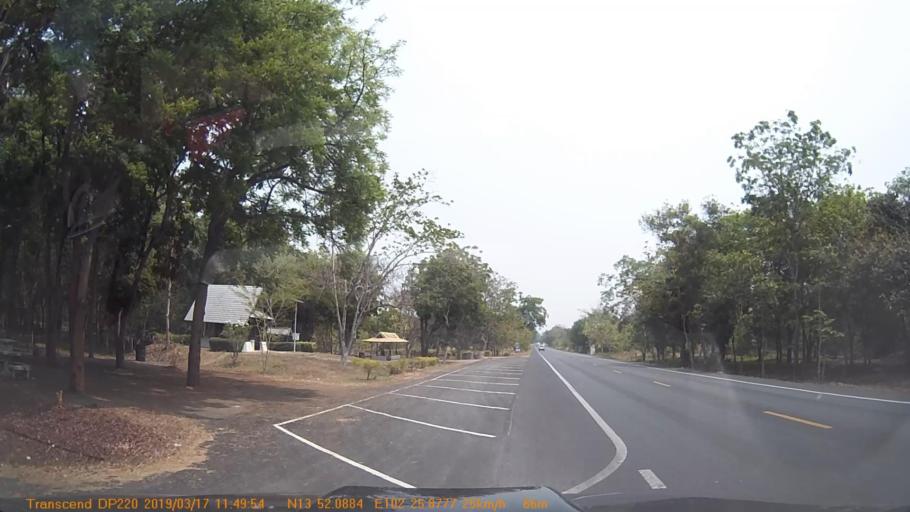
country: TH
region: Sa Kaeo
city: Watthana Nakhon
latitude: 13.8682
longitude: 102.4314
